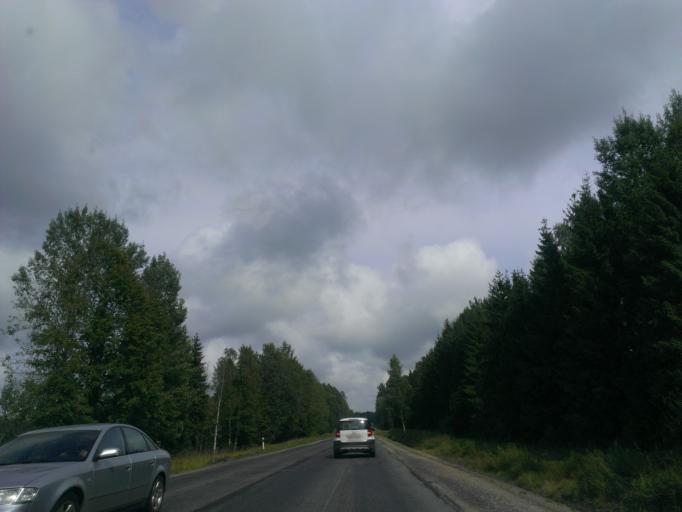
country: LV
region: Ligatne
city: Ligatne
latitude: 57.2014
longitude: 25.1228
